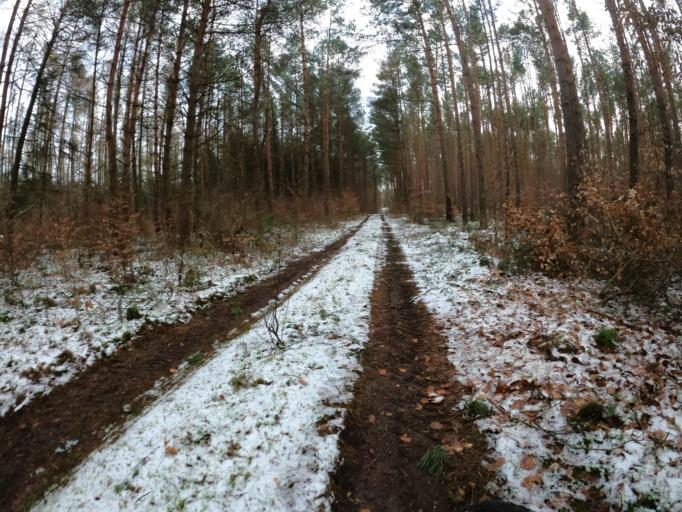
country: PL
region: Lubusz
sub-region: Powiat slubicki
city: Cybinka
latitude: 52.1928
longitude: 14.8693
